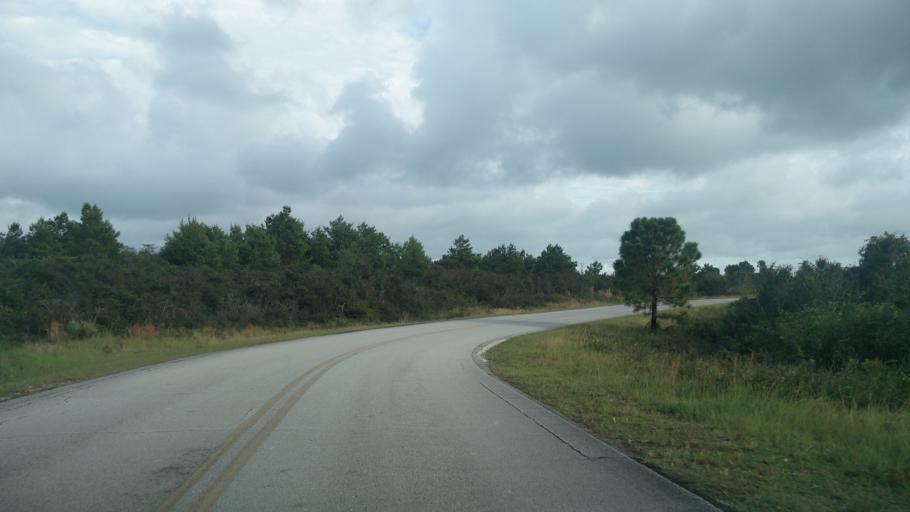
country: US
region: Florida
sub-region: Palm Beach County
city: Tequesta
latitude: 27.0090
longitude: -80.1056
